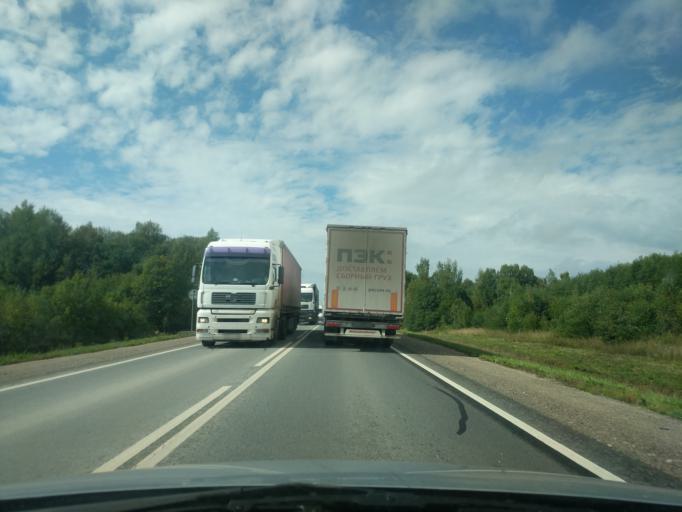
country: RU
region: Kostroma
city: Sudislavl'
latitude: 57.8630
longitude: 41.7667
